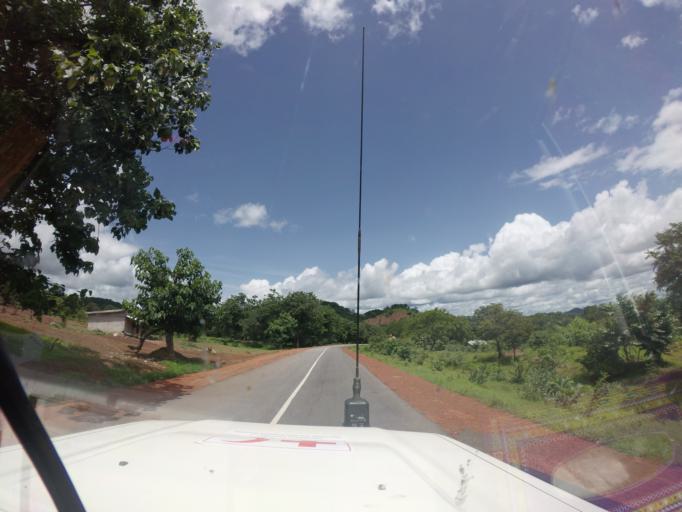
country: SL
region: Northern Province
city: Bindi
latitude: 10.1658
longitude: -11.4211
